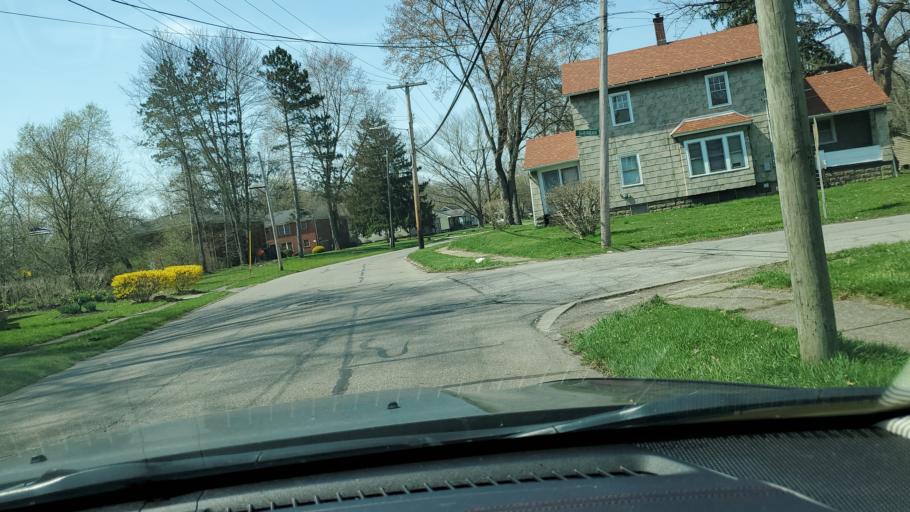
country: US
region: Ohio
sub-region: Trumbull County
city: Niles
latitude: 41.1724
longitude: -80.7700
